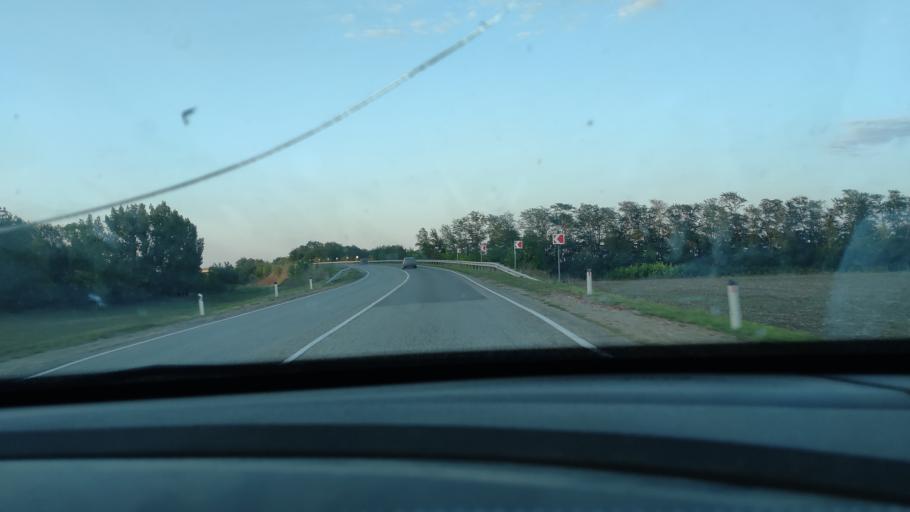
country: RU
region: Krasnodarskiy
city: Novominskaya
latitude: 46.4162
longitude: 39.0091
